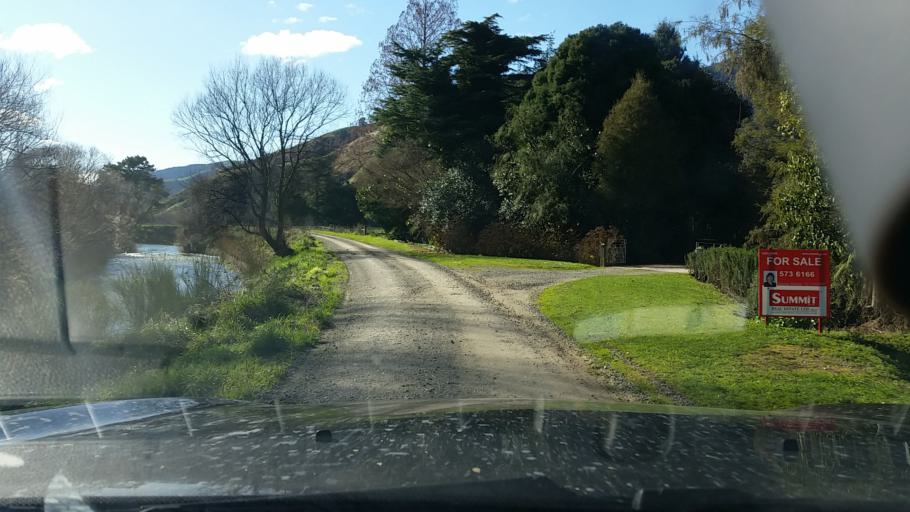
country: NZ
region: Marlborough
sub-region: Marlborough District
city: Picton
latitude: -41.3347
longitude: 173.7648
